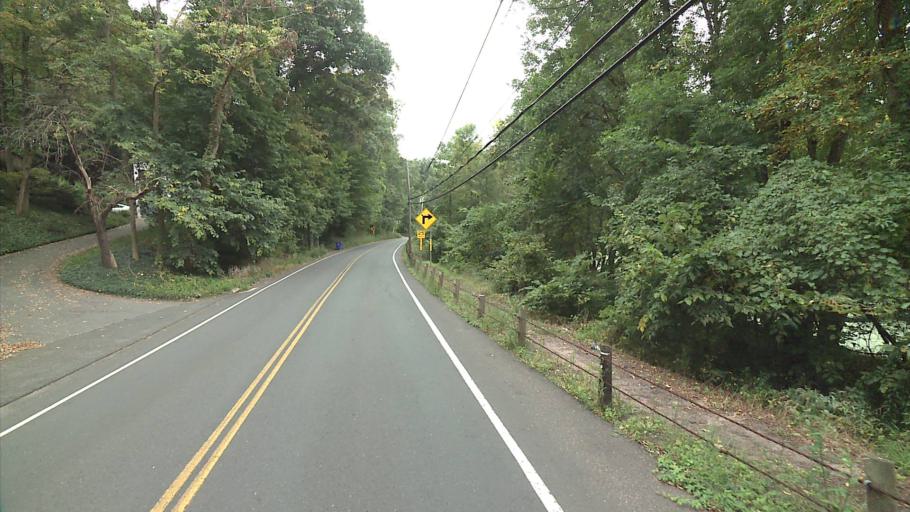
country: US
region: Connecticut
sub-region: Hartford County
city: Tariffville
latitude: 41.9004
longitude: -72.7742
